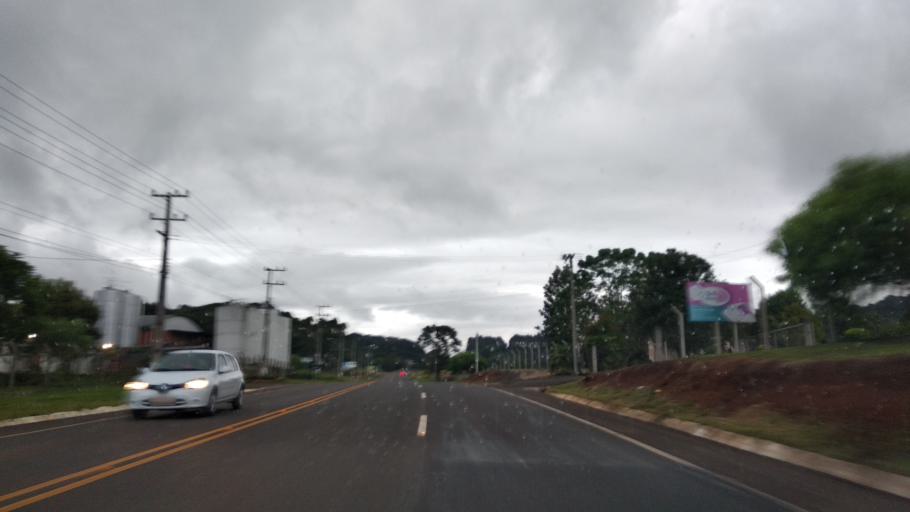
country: BR
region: Santa Catarina
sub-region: Videira
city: Videira
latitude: -27.0548
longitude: -51.1910
